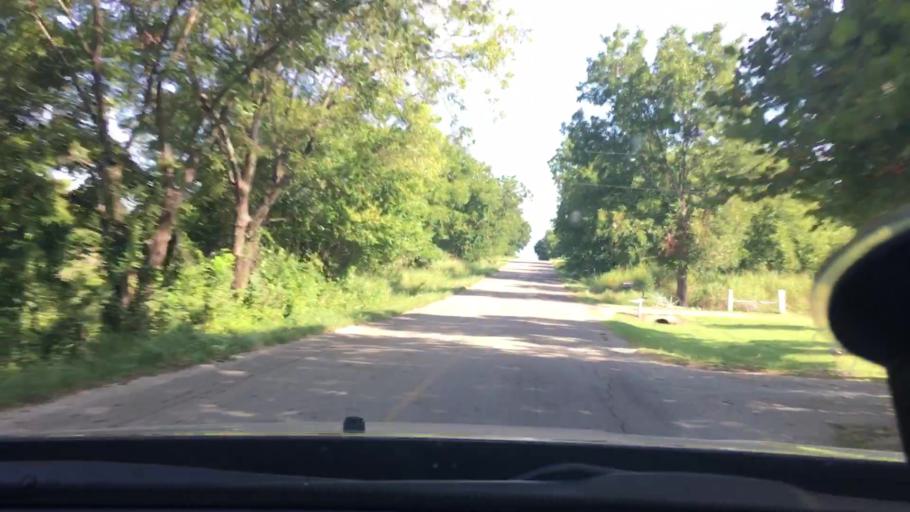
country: US
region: Oklahoma
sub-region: Carter County
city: Lone Grove
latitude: 34.2906
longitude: -97.2824
